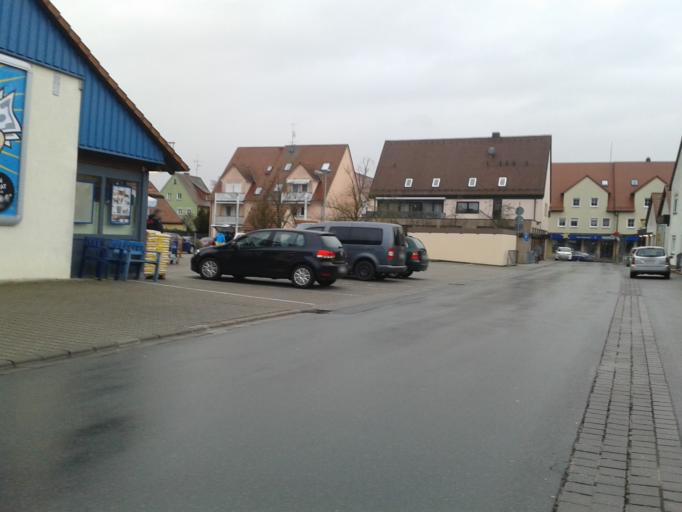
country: DE
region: Bavaria
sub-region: Regierungsbezirk Mittelfranken
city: Markt Erlbach
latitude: 49.4923
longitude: 10.6519
